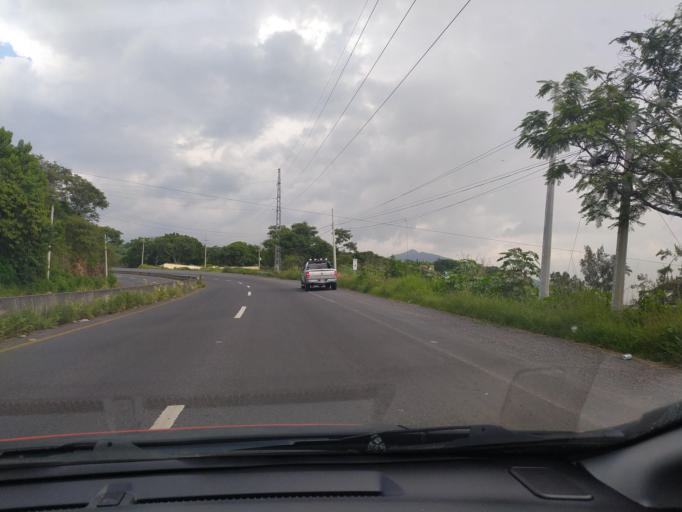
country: MX
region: Jalisco
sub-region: Acatlan de Juarez
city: Villa de los Ninos
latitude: 20.4294
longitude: -103.5847
